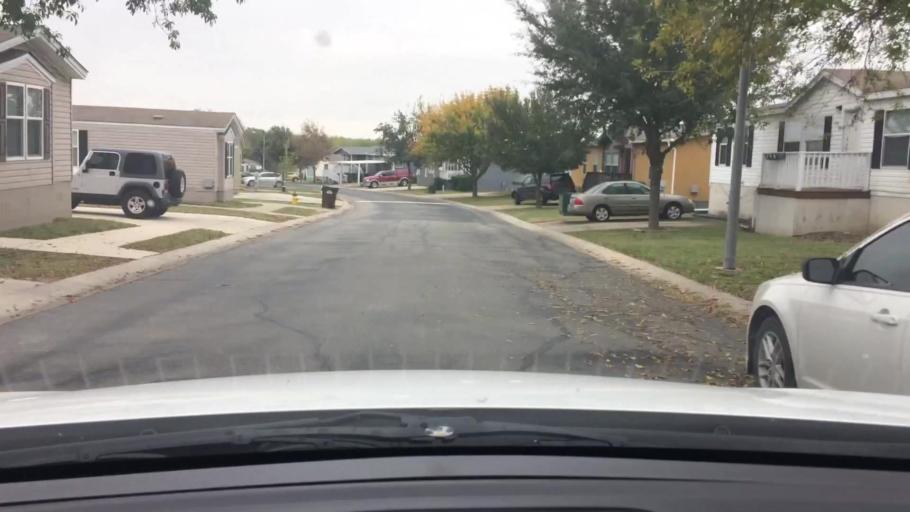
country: US
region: Texas
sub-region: Bexar County
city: Converse
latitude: 29.5254
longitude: -98.3397
